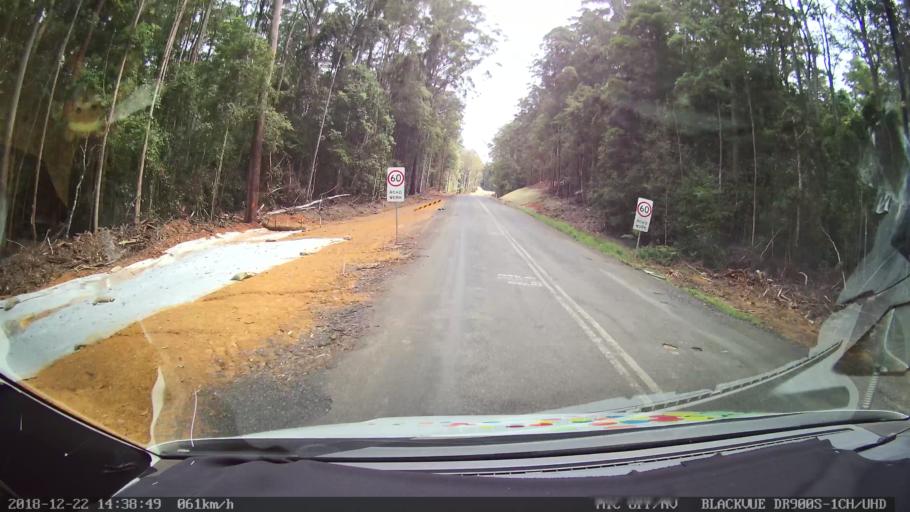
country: AU
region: New South Wales
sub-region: Bellingen
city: Dorrigo
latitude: -30.1412
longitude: 152.5952
